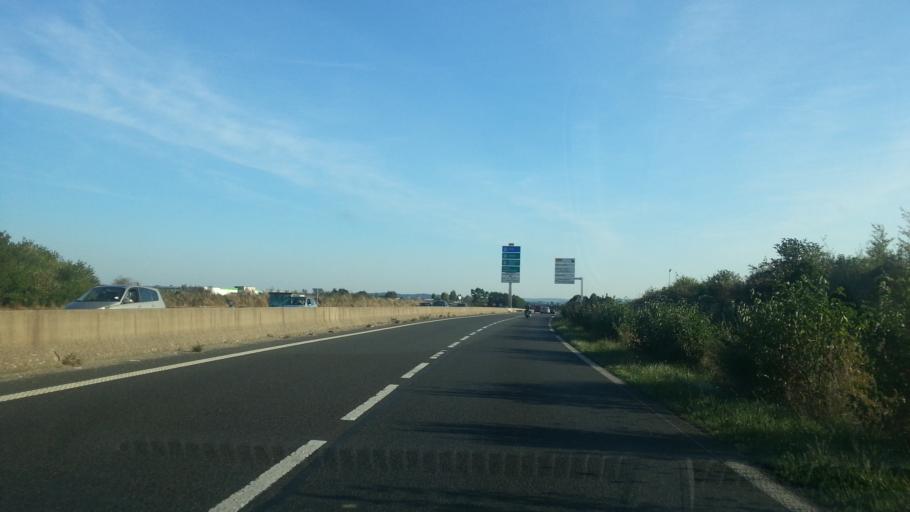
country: FR
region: Picardie
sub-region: Departement de l'Oise
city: Tille
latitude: 49.4424
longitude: 2.1118
